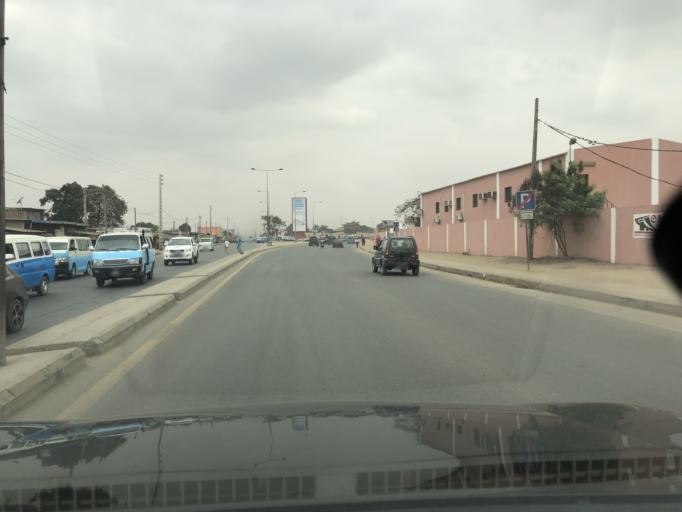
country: AO
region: Luanda
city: Luanda
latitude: -8.8231
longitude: 13.2822
